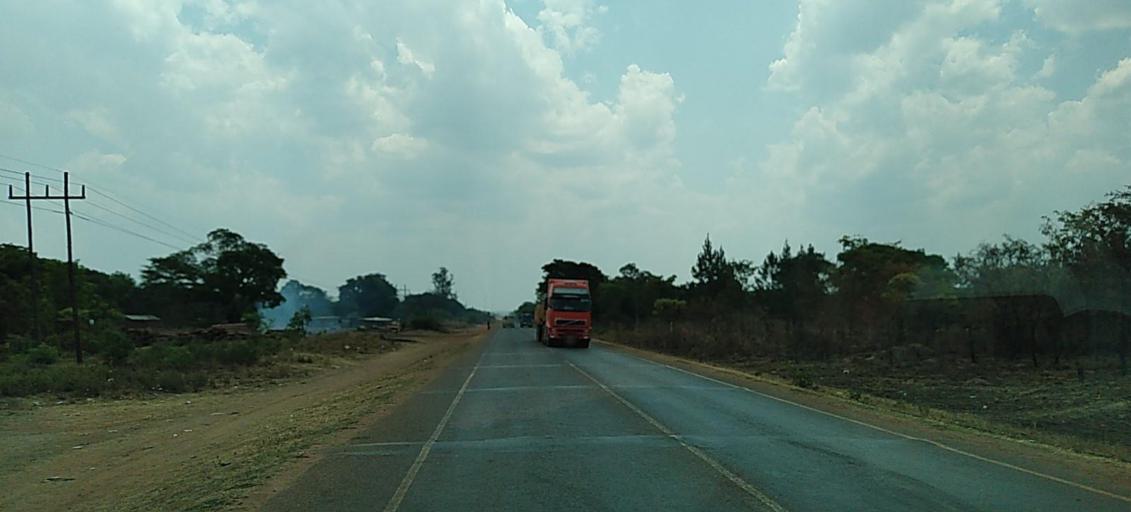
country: ZM
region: Copperbelt
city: Kalulushi
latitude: -12.8440
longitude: 28.0124
